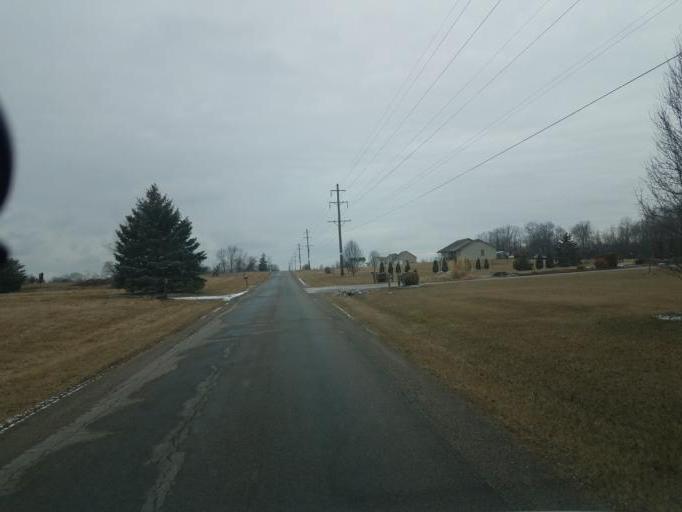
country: US
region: Ohio
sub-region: Defiance County
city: Hicksville
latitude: 41.3537
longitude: -84.7501
